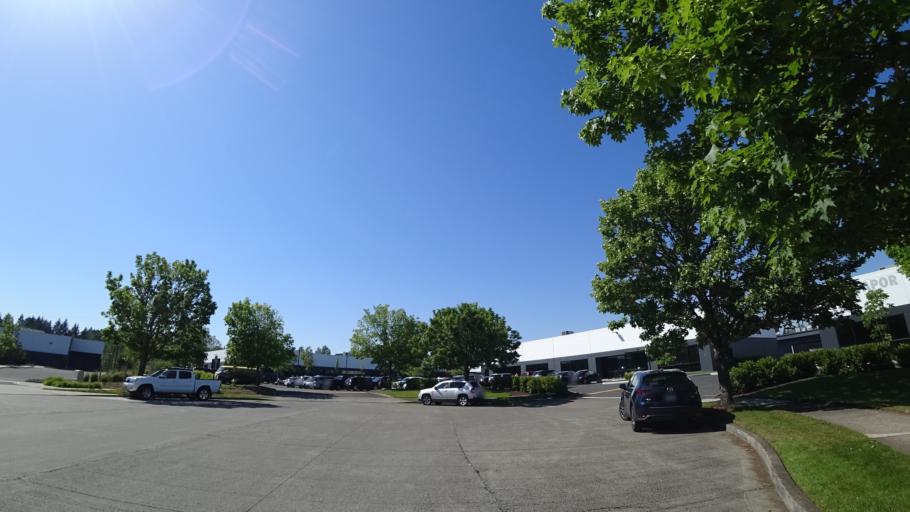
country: US
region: Oregon
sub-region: Washington County
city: Aloha
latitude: 45.4950
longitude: -122.8357
